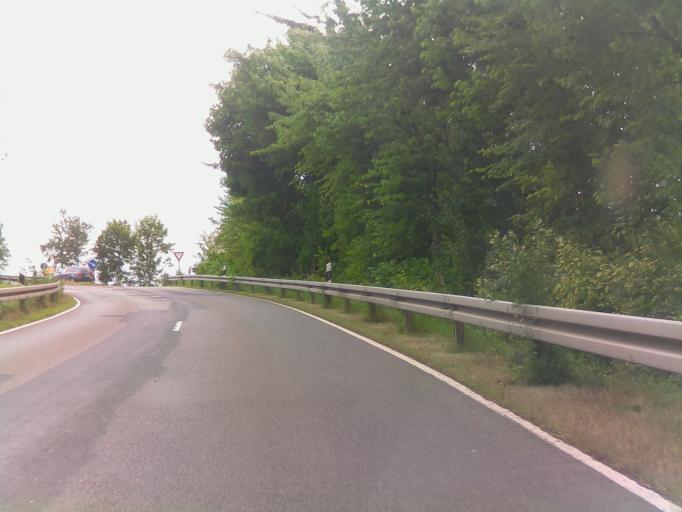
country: DE
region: Lower Saxony
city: Nordstemmen
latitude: 52.1455
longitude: 9.7618
